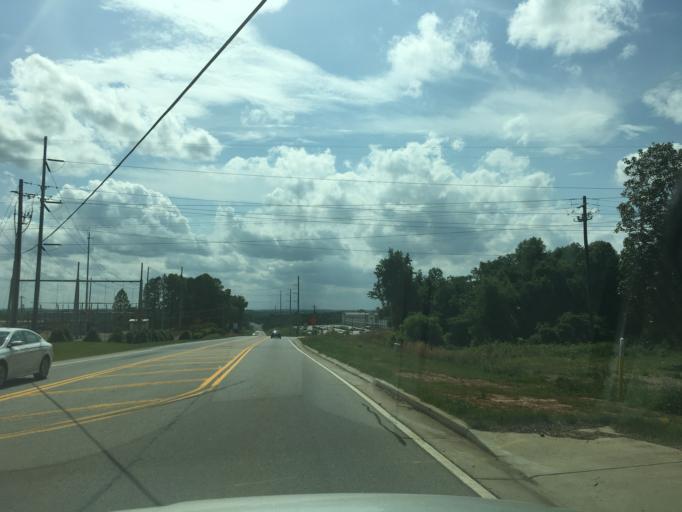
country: US
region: Georgia
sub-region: Jackson County
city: Braselton
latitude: 34.1071
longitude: -83.7686
